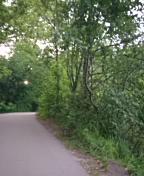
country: RU
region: Moscow
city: Pokrovskoye-Streshnevo
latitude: 55.8158
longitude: 37.4779
